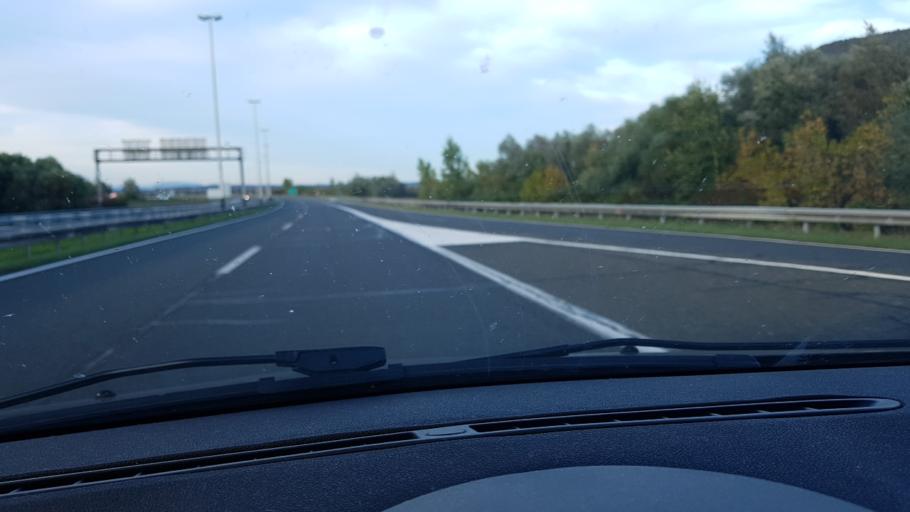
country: HR
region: Zagrebacka
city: Zapresic
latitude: 45.8577
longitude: 15.8296
